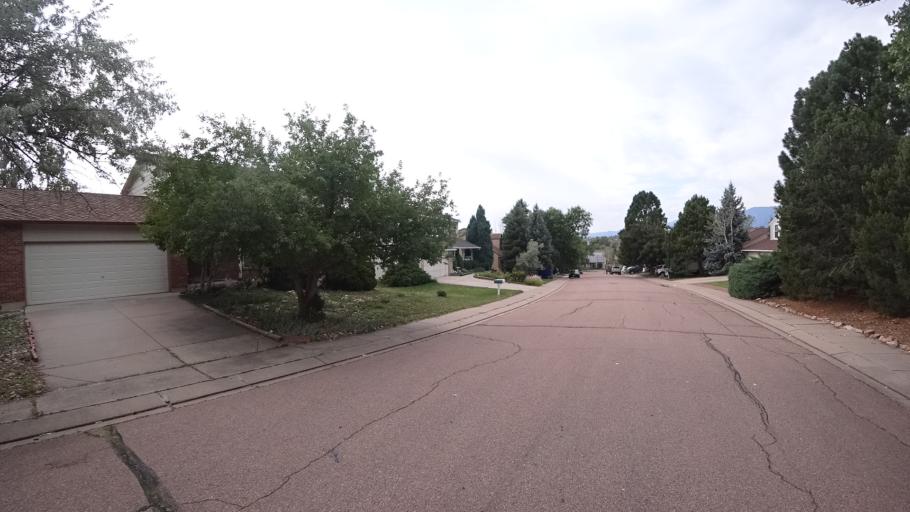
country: US
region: Colorado
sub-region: El Paso County
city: Air Force Academy
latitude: 38.9239
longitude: -104.8342
